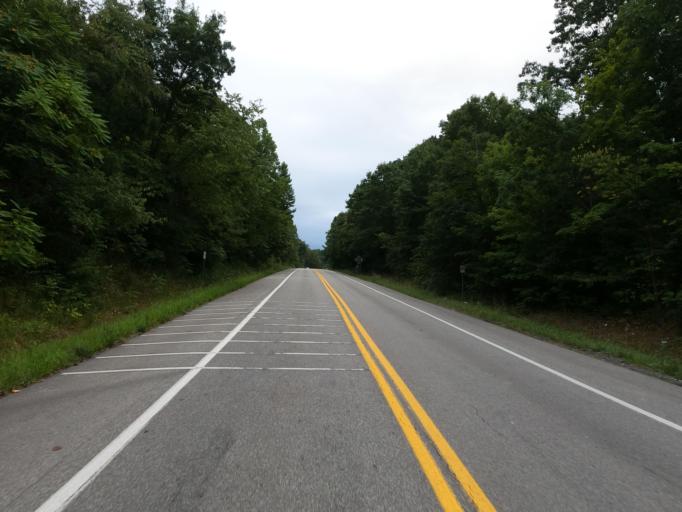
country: US
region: West Virginia
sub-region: Marion County
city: Fairmont
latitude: 39.4944
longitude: -80.0915
